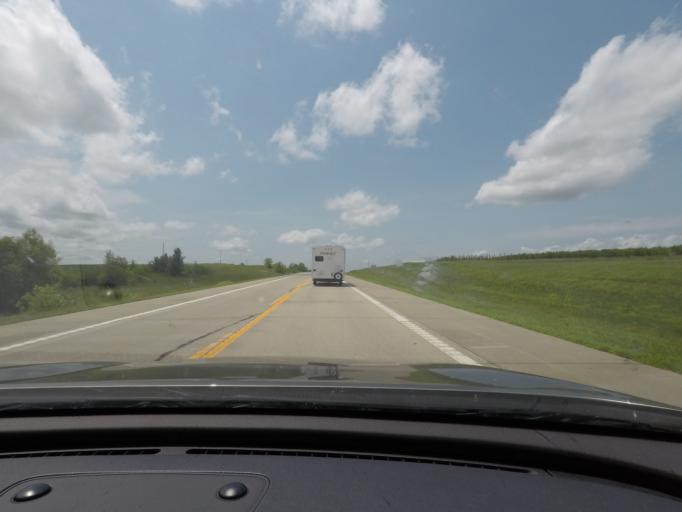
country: US
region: Missouri
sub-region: Carroll County
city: Carrollton
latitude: 39.2021
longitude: -93.4863
